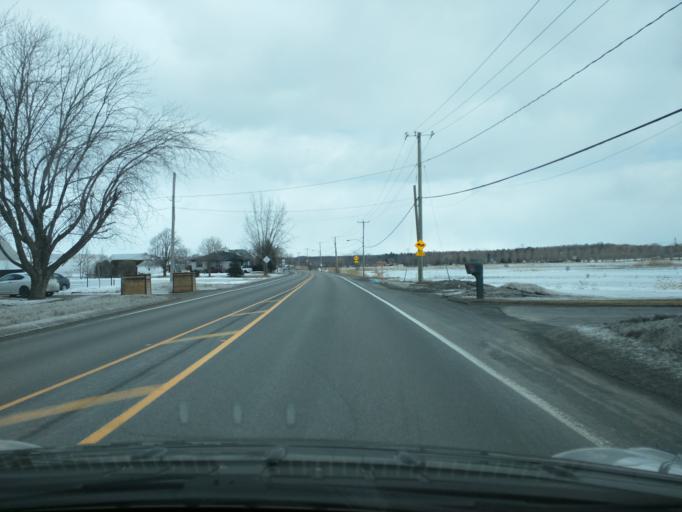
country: CA
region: Quebec
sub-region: Monteregie
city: Sainte-Julie
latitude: 45.6150
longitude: -73.3656
